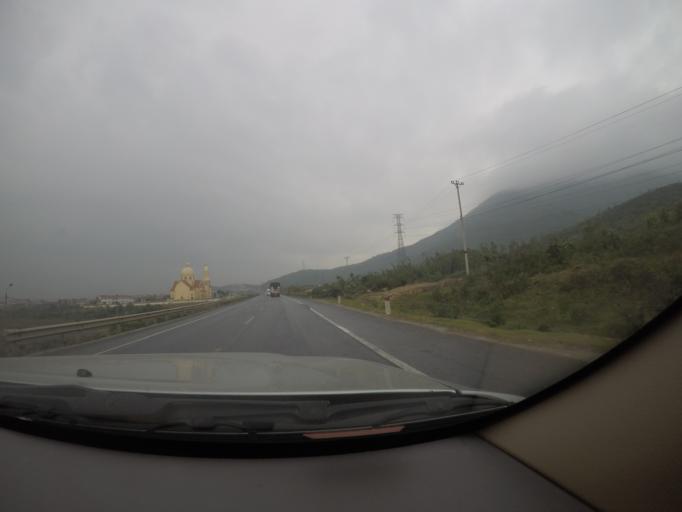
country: VN
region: Ha Tinh
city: Ky Anh
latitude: 17.9973
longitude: 106.4543
